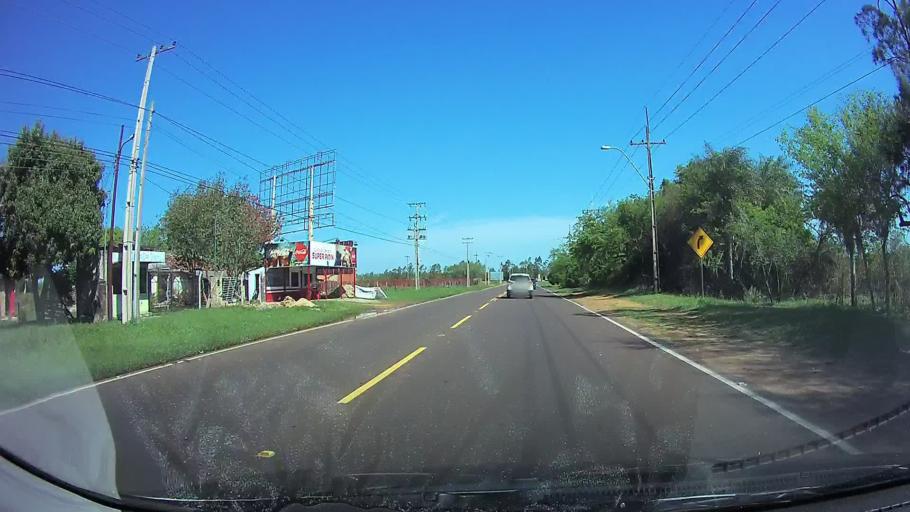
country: PY
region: Central
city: Ypacarai
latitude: -25.3619
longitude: -57.2652
